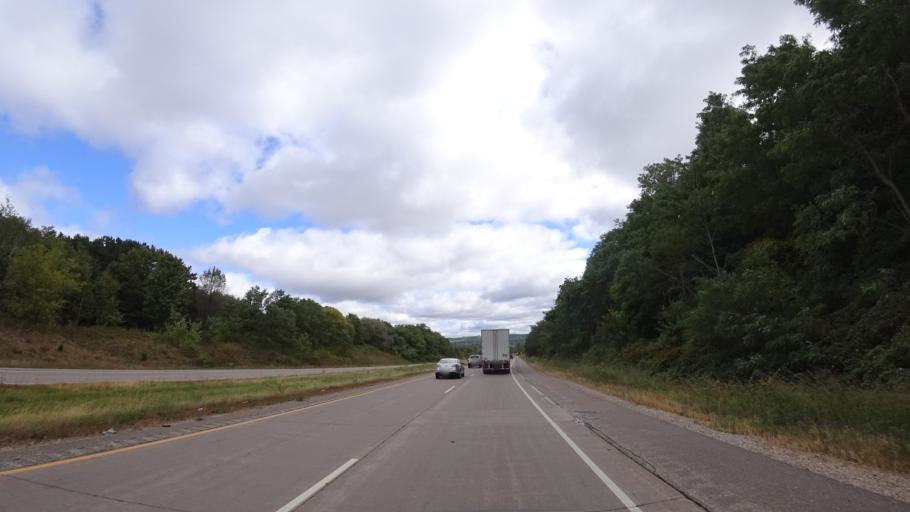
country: US
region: Wisconsin
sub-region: Eau Claire County
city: Eau Claire
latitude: 44.8424
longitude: -91.5170
